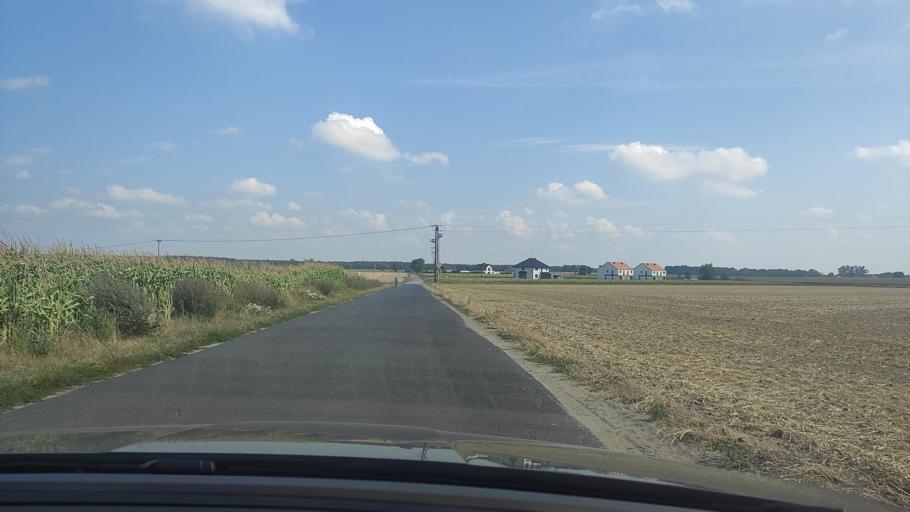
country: PL
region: Greater Poland Voivodeship
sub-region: Powiat poznanski
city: Kostrzyn
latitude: 52.4817
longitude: 17.1898
